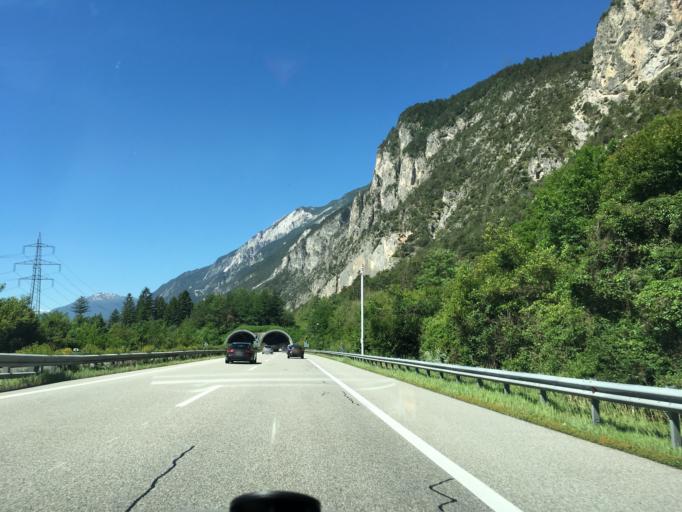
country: AT
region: Tyrol
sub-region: Politischer Bezirk Imst
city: Haiming
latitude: 47.2646
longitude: 10.8898
